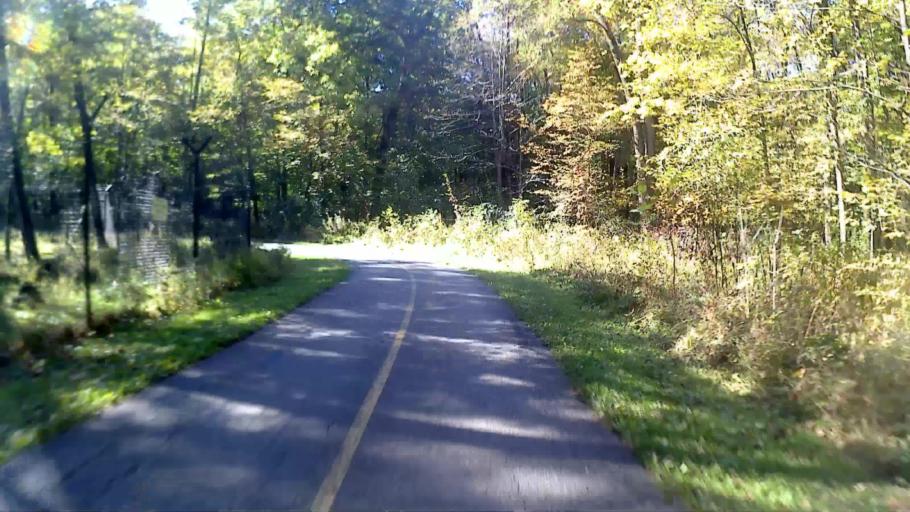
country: US
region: Illinois
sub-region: Cook County
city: Elk Grove Village
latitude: 42.0321
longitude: -87.9899
